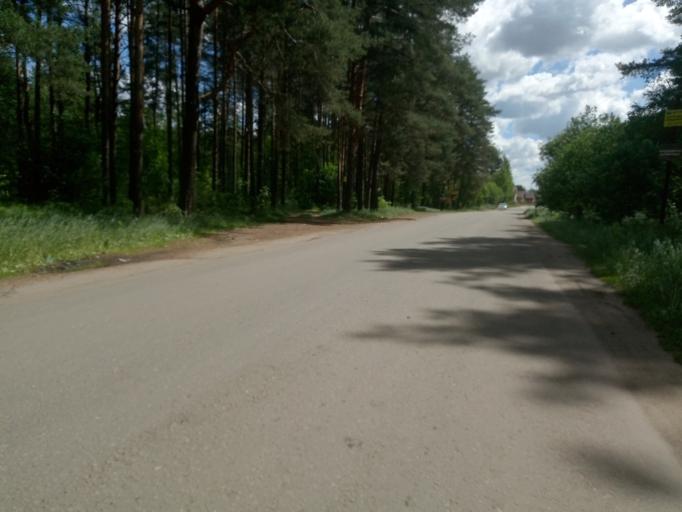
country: RU
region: Jaroslavl
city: Yaroslavl
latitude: 57.6549
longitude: 39.9842
